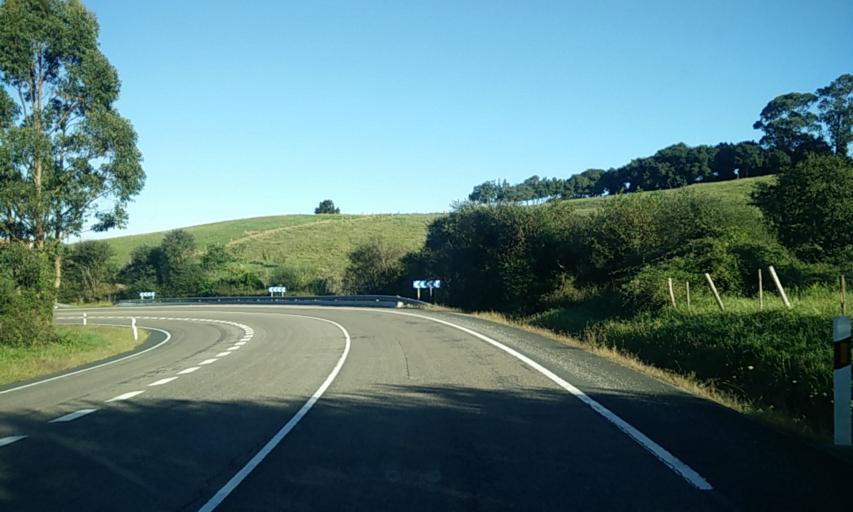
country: ES
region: Cantabria
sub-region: Provincia de Cantabria
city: San Vicente de la Barquera
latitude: 43.3829
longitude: -4.3825
